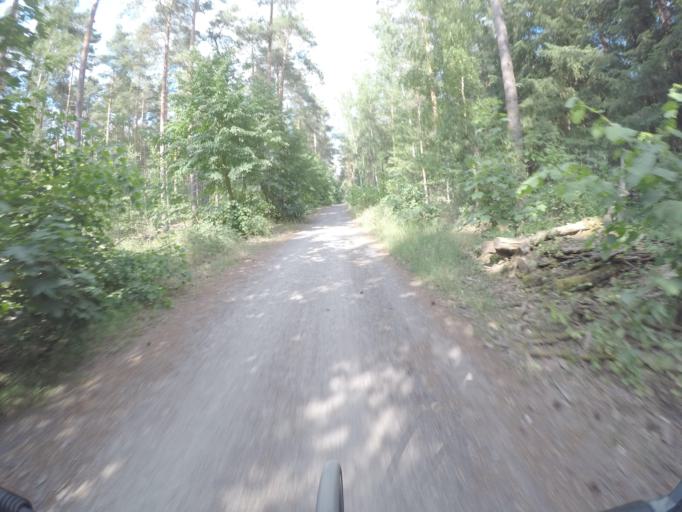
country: DE
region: Berlin
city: Wannsee
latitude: 52.4014
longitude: 13.1550
